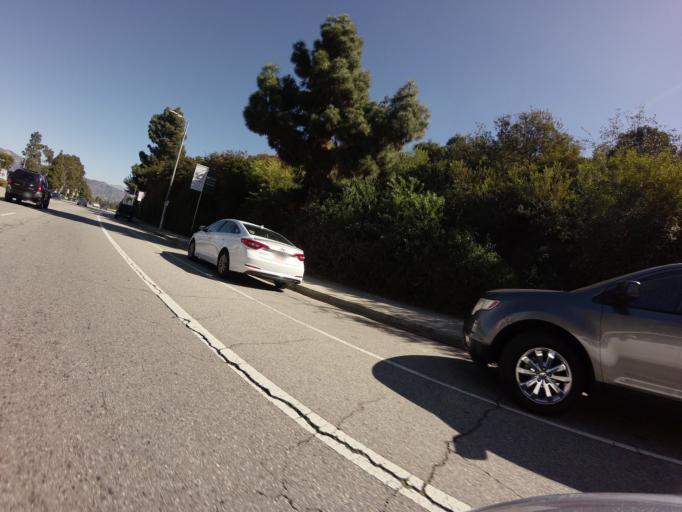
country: US
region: California
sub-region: Los Angeles County
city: Universal City
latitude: 34.1442
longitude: -118.3396
